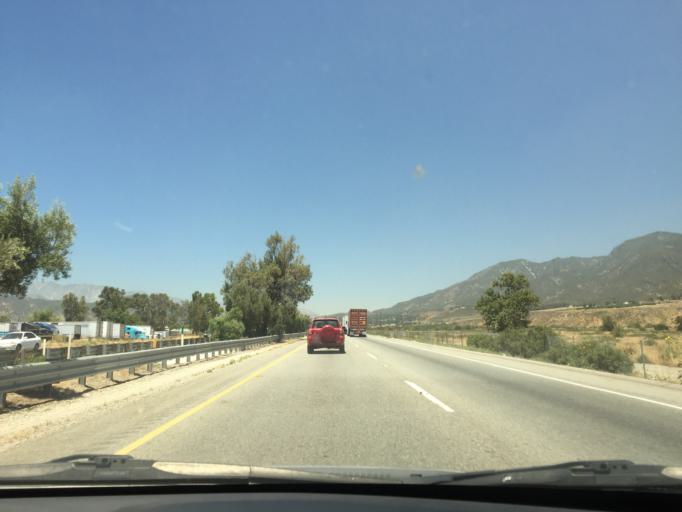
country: US
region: California
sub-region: San Bernardino County
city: Muscoy
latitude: 34.2024
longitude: -117.3760
